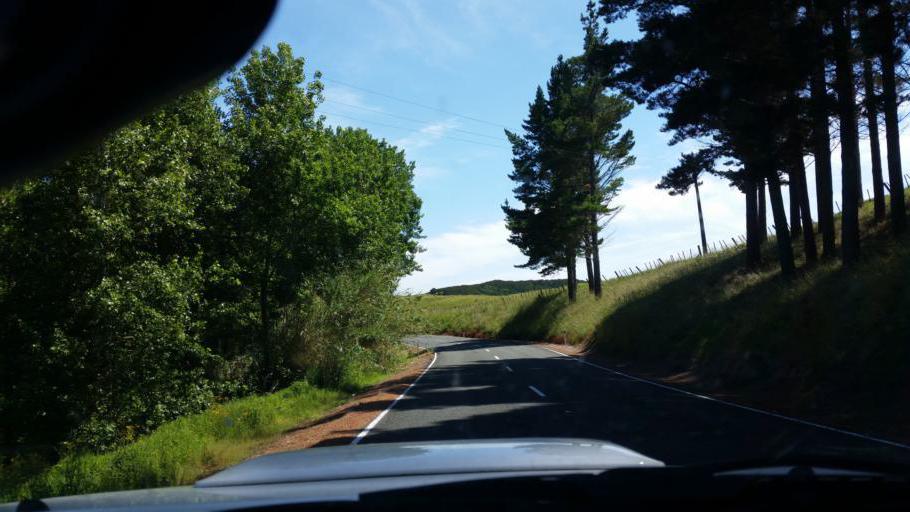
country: NZ
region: Auckland
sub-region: Auckland
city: Wellsford
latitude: -36.2015
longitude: 174.3964
